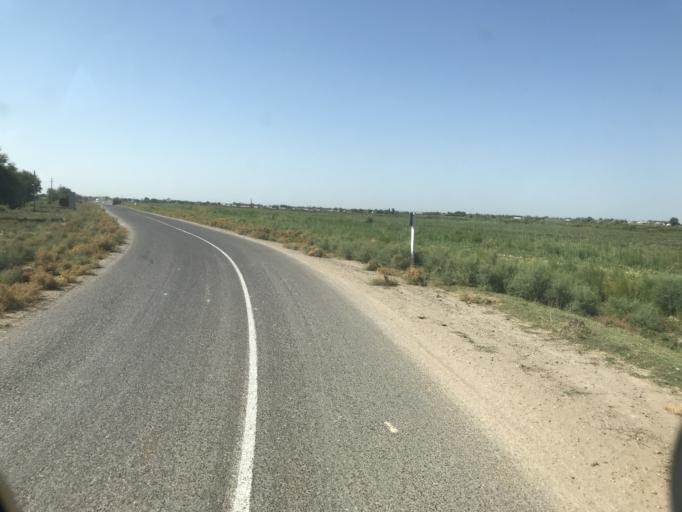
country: KZ
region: Ongtustik Qazaqstan
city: Myrzakent
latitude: 40.6828
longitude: 68.5570
